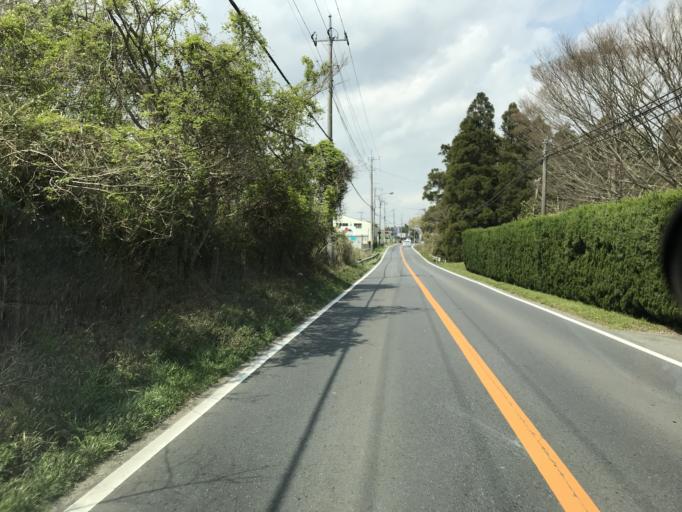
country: JP
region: Chiba
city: Sawara
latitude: 35.8597
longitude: 140.5527
